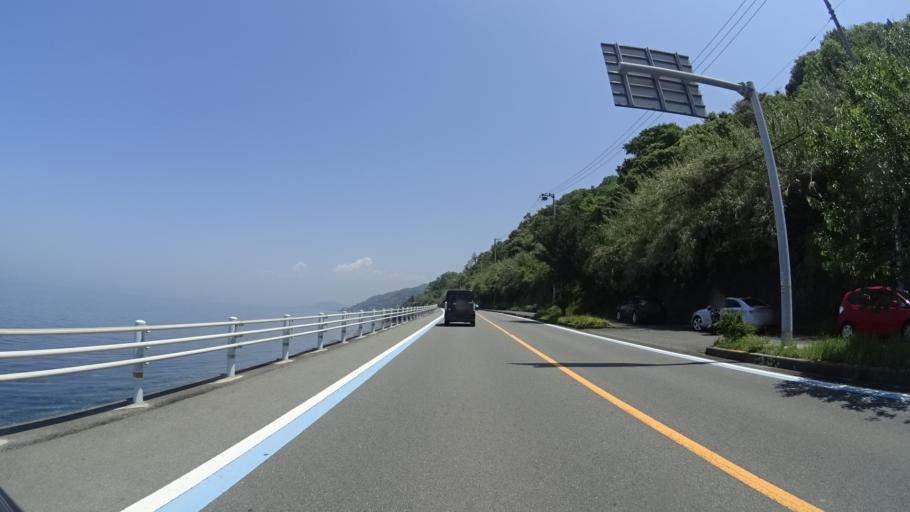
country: JP
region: Ehime
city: Iyo
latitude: 33.6583
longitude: 132.5931
